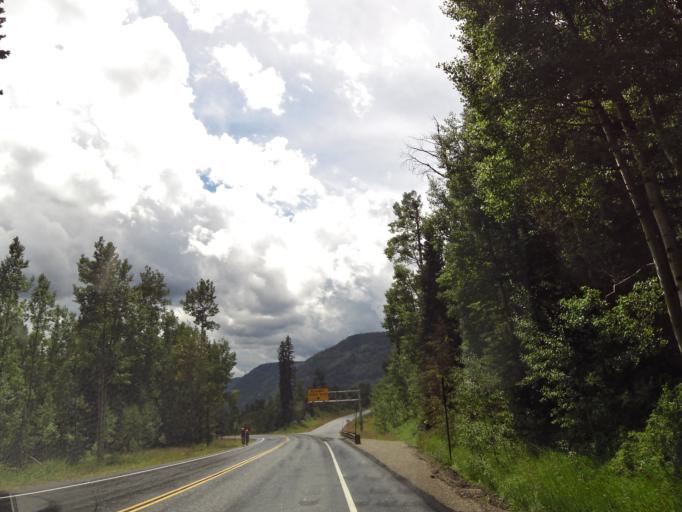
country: US
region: Colorado
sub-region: San Juan County
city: Silverton
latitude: 37.6663
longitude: -107.7973
